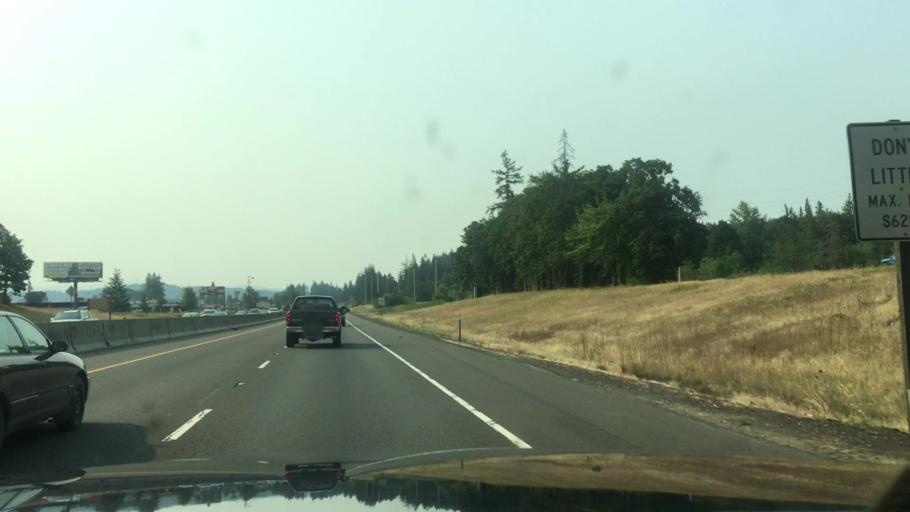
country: US
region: Oregon
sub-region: Lane County
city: Springfield
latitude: 44.0136
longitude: -123.0235
